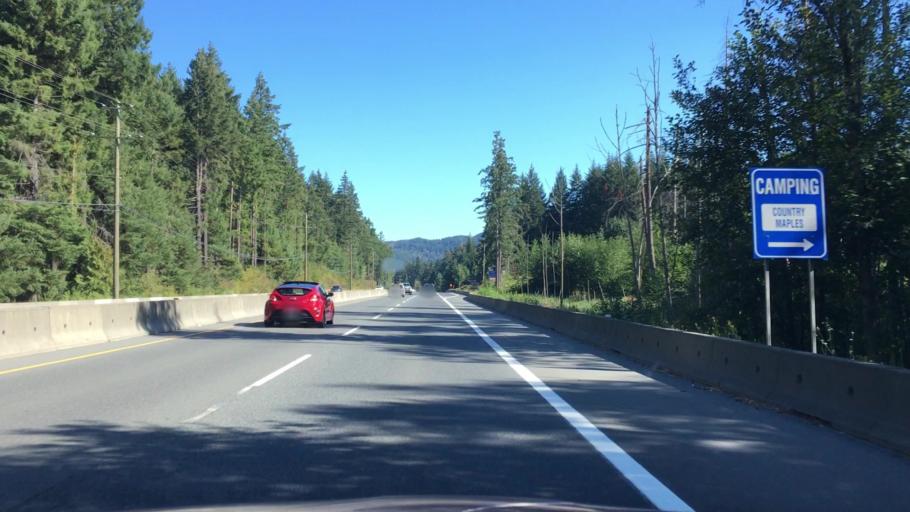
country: CA
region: British Columbia
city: North Cowichan
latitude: 48.8980
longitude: -123.7165
